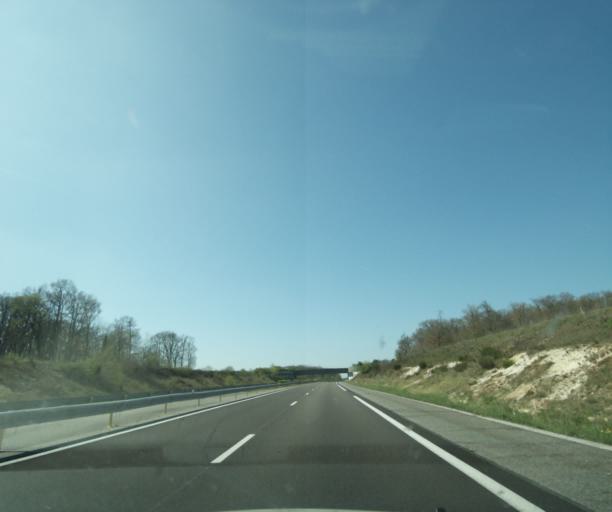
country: FR
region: Centre
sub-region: Departement du Loiret
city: Bonny-sur-Loire
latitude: 47.6114
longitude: 2.8220
